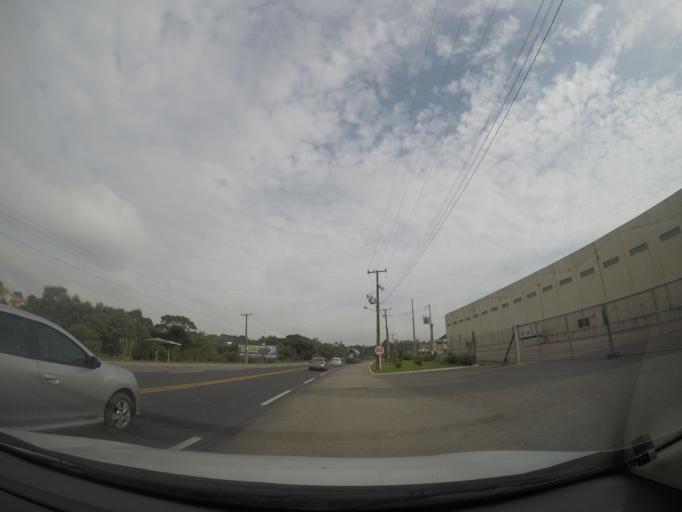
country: BR
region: Parana
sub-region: Colombo
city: Colombo
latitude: -25.3431
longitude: -49.2346
